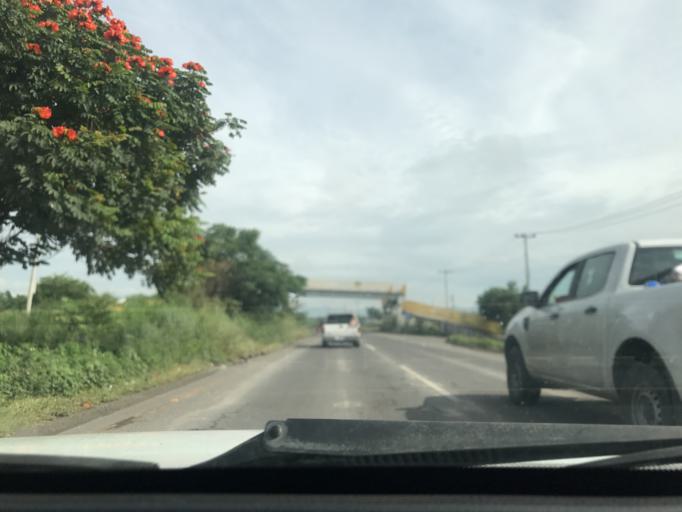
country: MX
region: Morelos
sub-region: Yecapixtla
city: Juan Morales
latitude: 18.8287
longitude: -98.9219
